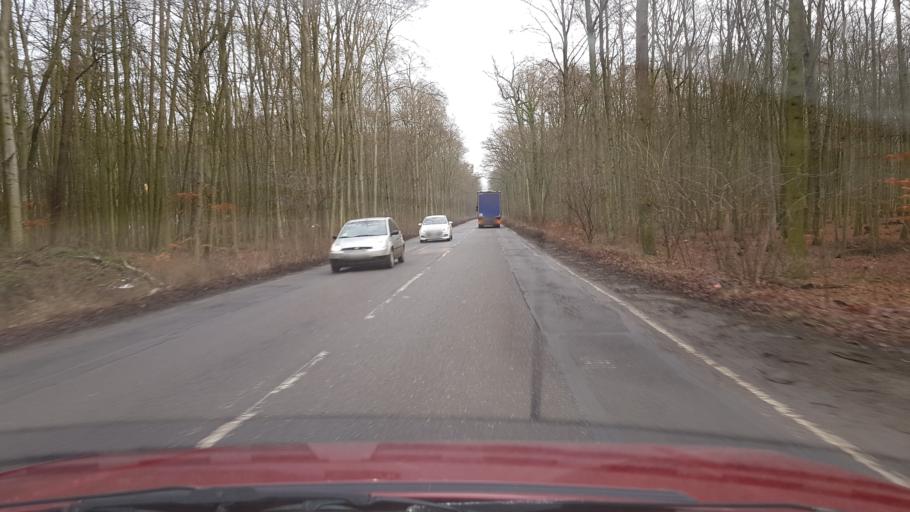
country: PL
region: West Pomeranian Voivodeship
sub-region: Powiat policki
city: Police
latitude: 53.5299
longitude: 14.5733
